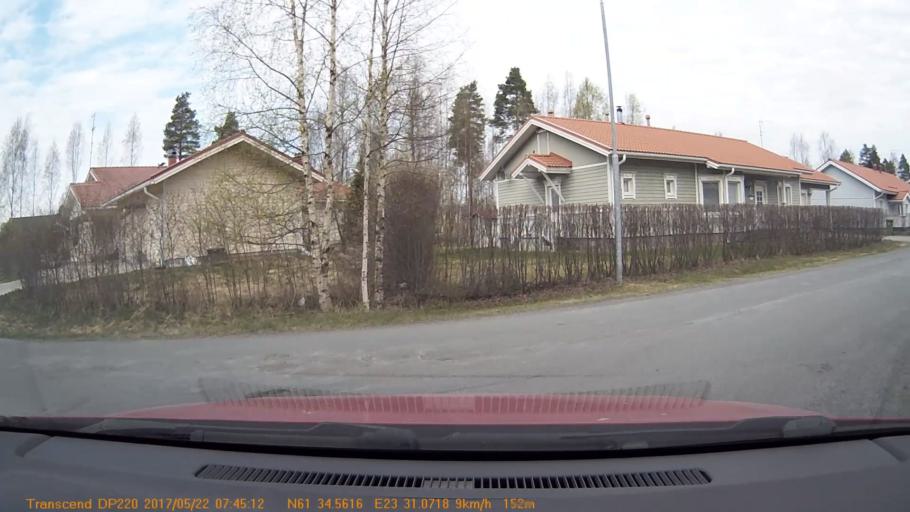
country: FI
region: Pirkanmaa
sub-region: Tampere
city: Yloejaervi
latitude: 61.5758
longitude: 23.5179
